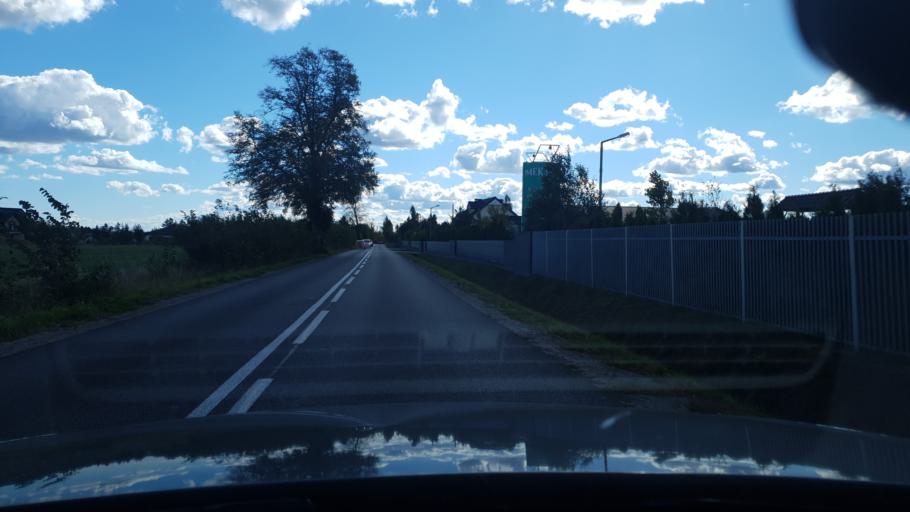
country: PL
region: Pomeranian Voivodeship
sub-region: Powiat pucki
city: Zelistrzewo
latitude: 54.6963
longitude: 18.4121
